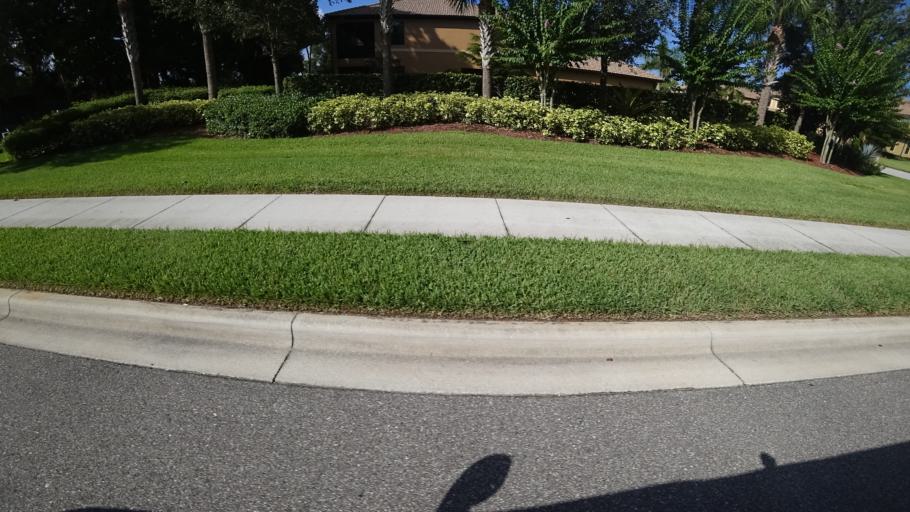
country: US
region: Florida
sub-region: Manatee County
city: Ellenton
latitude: 27.5050
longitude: -82.4743
